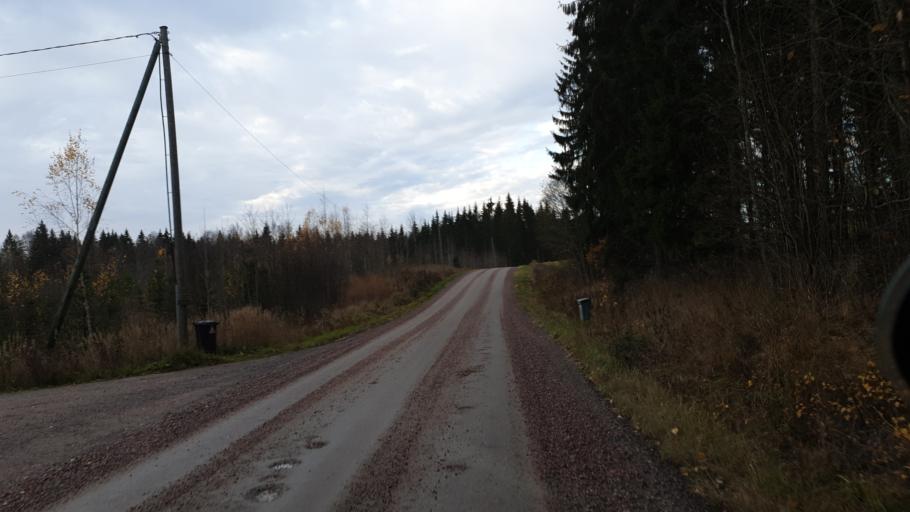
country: FI
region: Uusimaa
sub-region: Helsinki
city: Siuntio
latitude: 60.1505
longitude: 24.2760
